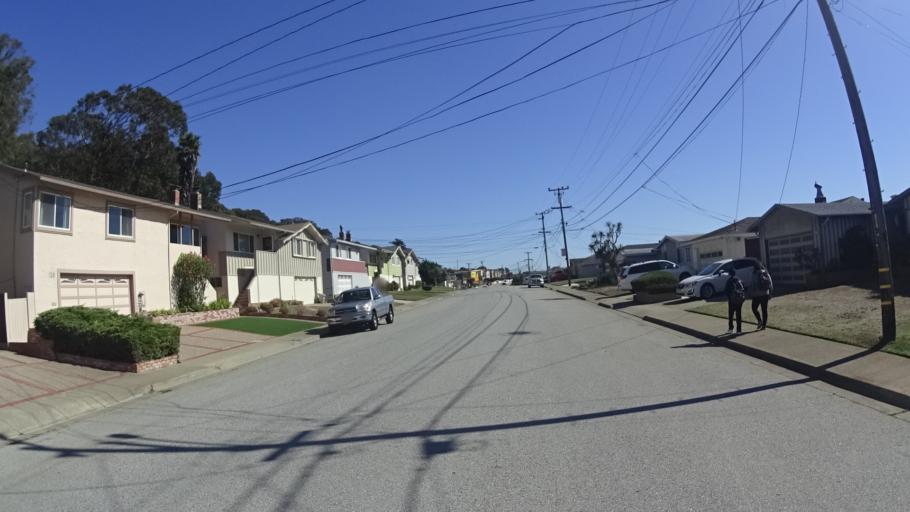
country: US
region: California
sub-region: San Mateo County
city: South San Francisco
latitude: 37.6623
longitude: -122.4236
